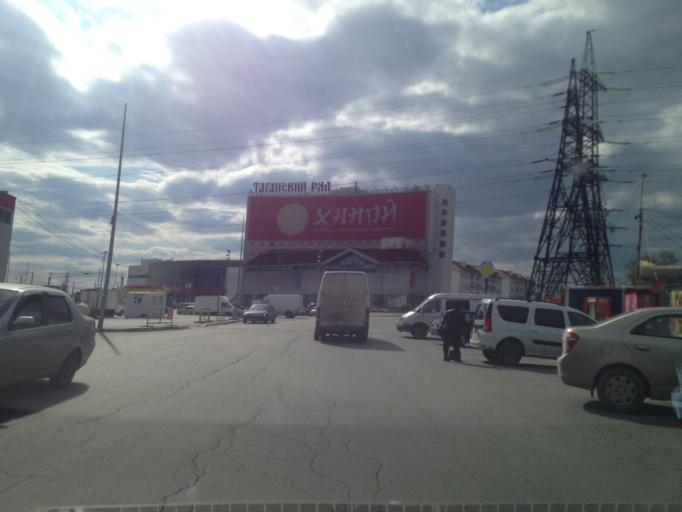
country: RU
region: Sverdlovsk
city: Yekaterinburg
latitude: 56.8615
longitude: 60.5400
